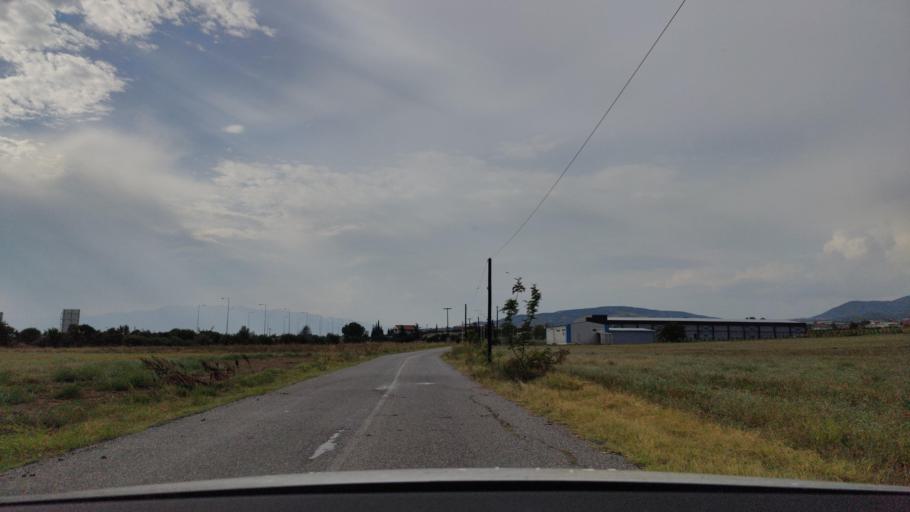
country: GR
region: Central Macedonia
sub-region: Nomos Serron
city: Kala Dendra
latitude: 41.1339
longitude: 23.4426
